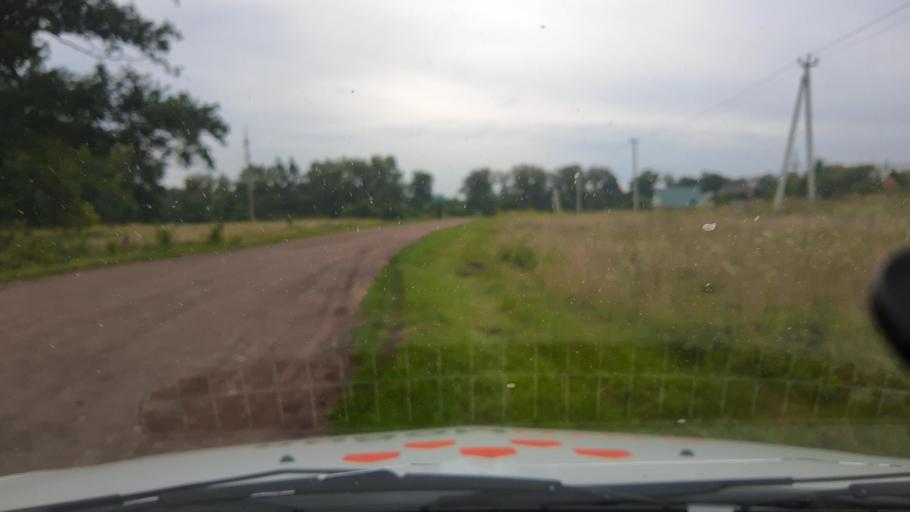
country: RU
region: Bashkortostan
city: Ufa
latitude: 54.5709
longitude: 55.9493
